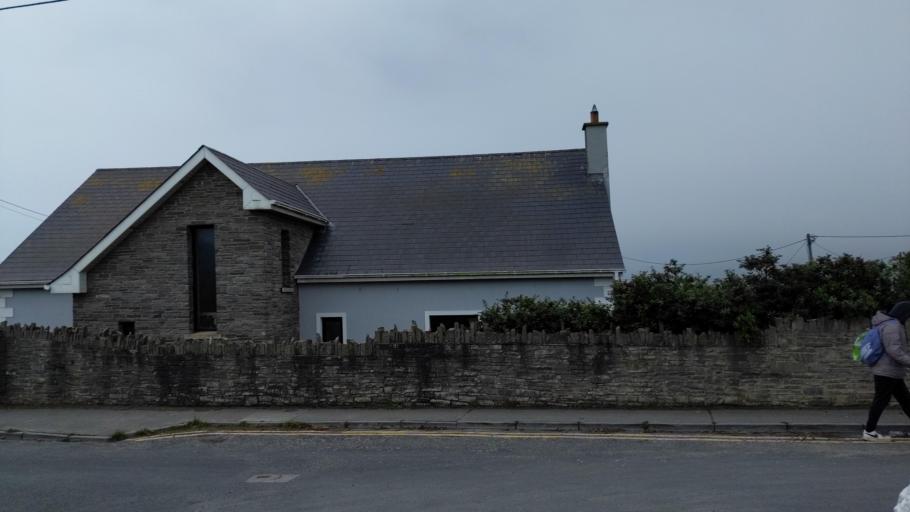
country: IE
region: Leinster
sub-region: Lu
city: Clogherhead
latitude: 53.7896
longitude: -6.2342
